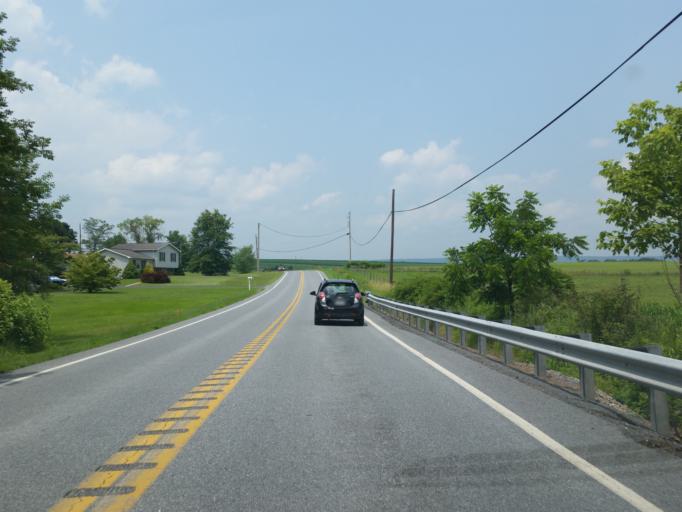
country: US
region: Pennsylvania
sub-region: Lebanon County
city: Palmyra
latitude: 40.3592
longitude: -76.6205
